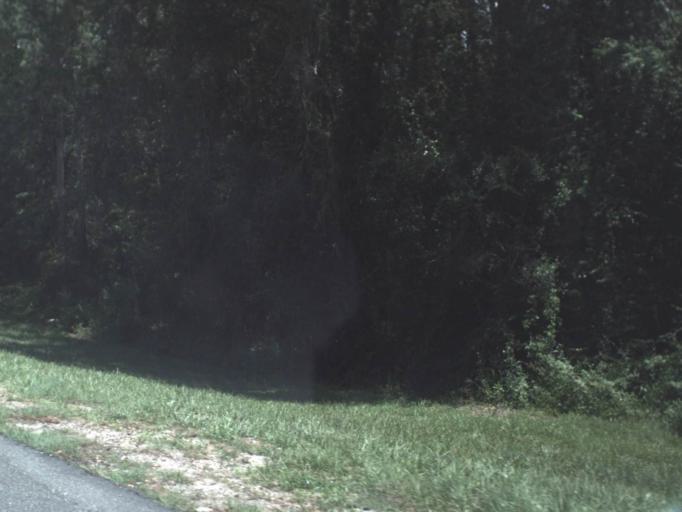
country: US
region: Florida
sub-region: Taylor County
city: Perry
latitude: 30.0942
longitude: -83.4885
